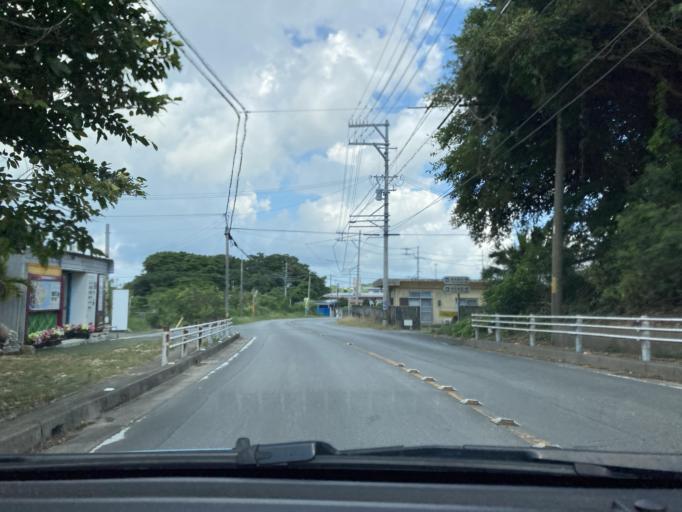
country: JP
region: Okinawa
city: Tomigusuku
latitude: 26.1477
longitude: 127.7914
